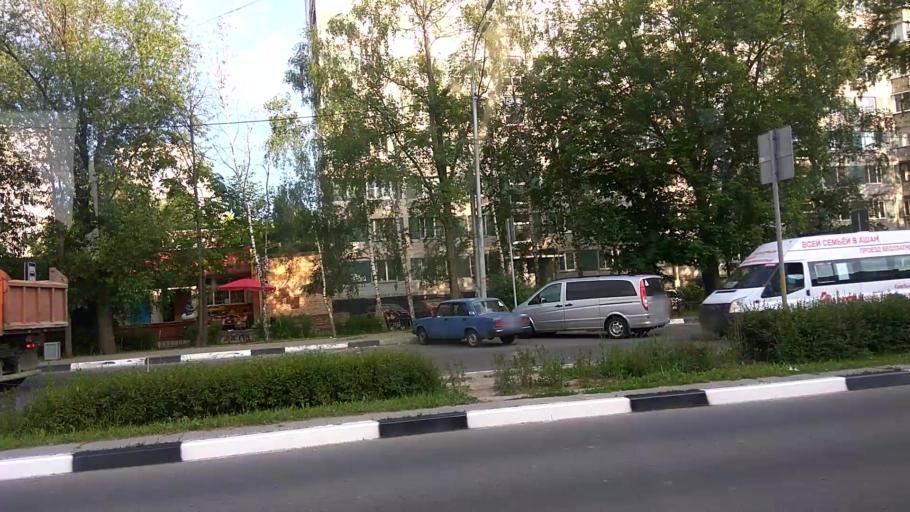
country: RU
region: Moskovskaya
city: Mytishchi
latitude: 55.9075
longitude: 37.7101
